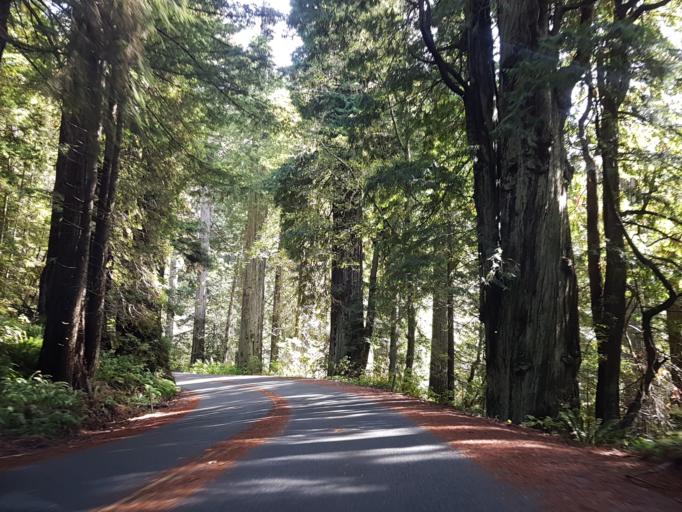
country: US
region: California
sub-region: Del Norte County
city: Bertsch-Oceanview
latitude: 41.4522
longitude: -124.0415
